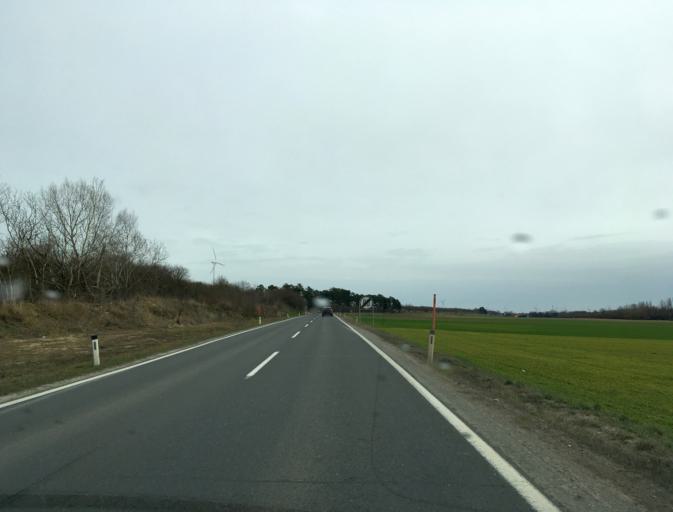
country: AT
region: Lower Austria
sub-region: Politischer Bezirk Ganserndorf
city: Deutsch-Wagram
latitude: 48.2876
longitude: 16.5675
